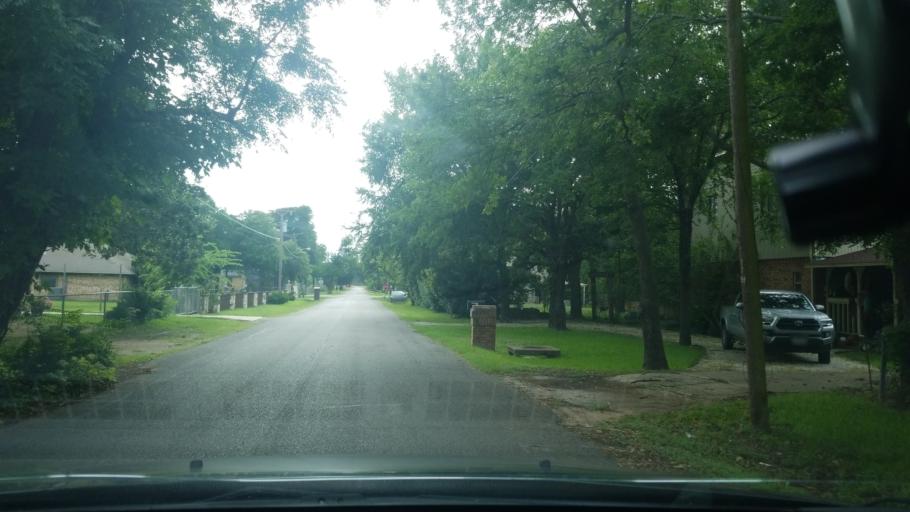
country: US
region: Texas
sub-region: Dallas County
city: Balch Springs
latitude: 32.7554
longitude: -96.6326
